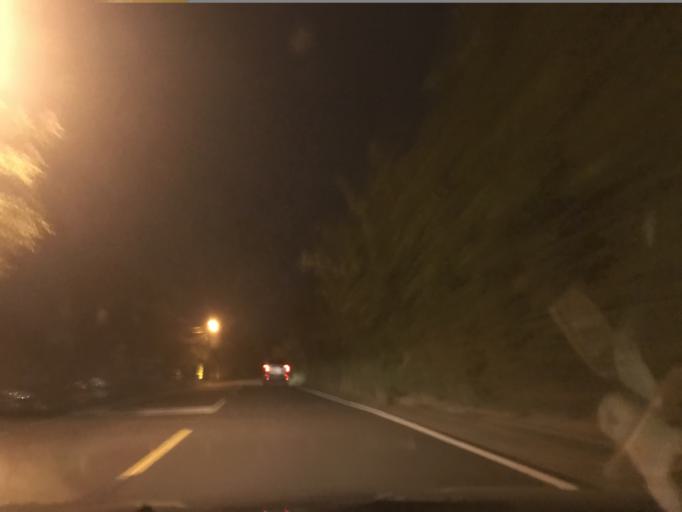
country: TW
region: Taiwan
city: Daxi
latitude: 24.9352
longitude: 121.2173
